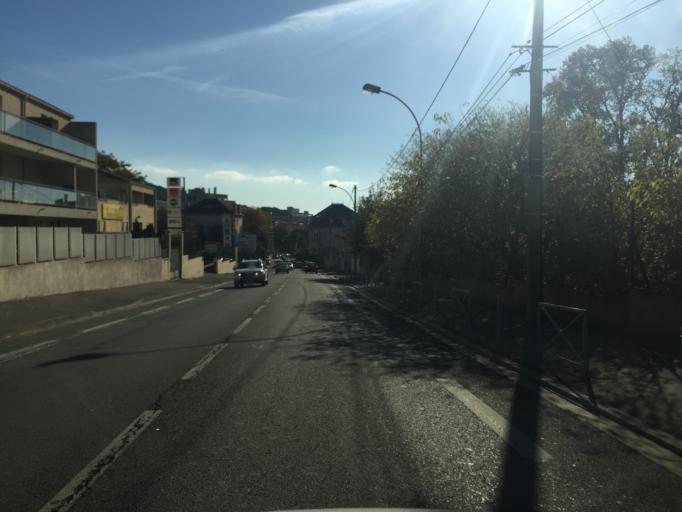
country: FR
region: Provence-Alpes-Cote d'Azur
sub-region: Departement des Bouches-du-Rhone
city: Salon-de-Provence
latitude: 43.6432
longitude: 5.1026
